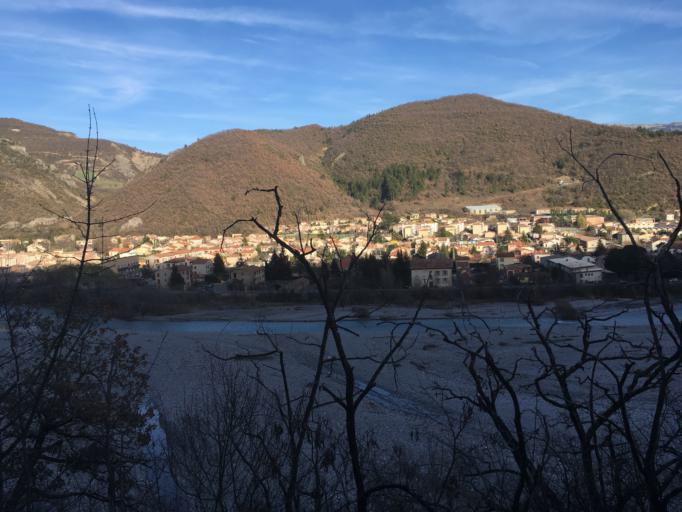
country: FR
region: Provence-Alpes-Cote d'Azur
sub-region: Departement des Alpes-de-Haute-Provence
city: Digne-les-Bains
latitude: 44.1047
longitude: 6.2262
